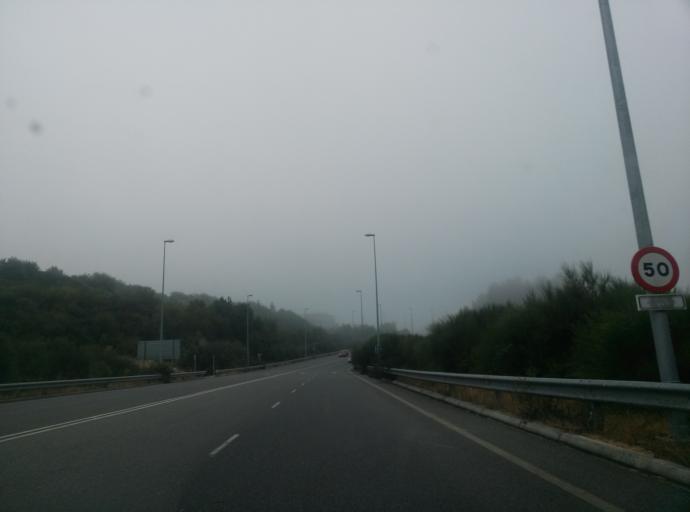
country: ES
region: Galicia
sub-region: Provincia de Lugo
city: Lugo
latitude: 43.0254
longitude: -7.5327
